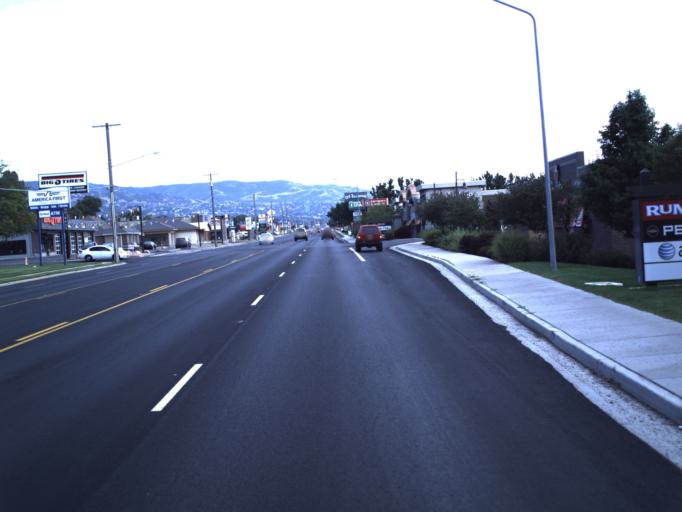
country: US
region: Utah
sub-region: Davis County
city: West Bountiful
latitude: 40.8902
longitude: -111.8923
